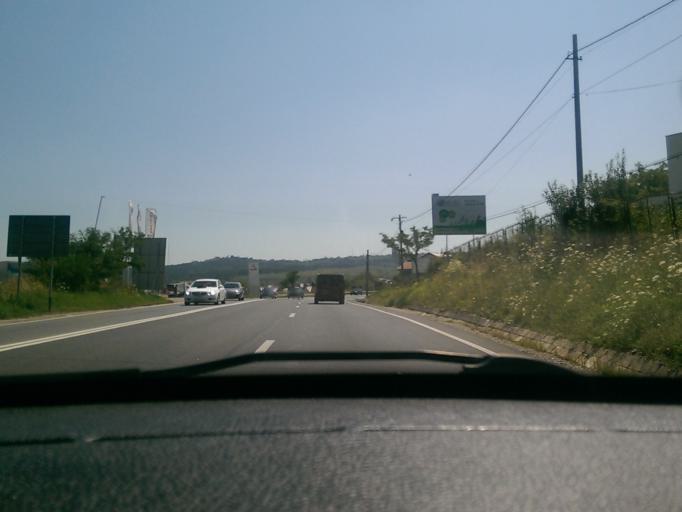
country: RO
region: Cluj
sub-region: Comuna Feleacu
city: Feleacu
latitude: 46.7364
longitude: 23.5933
